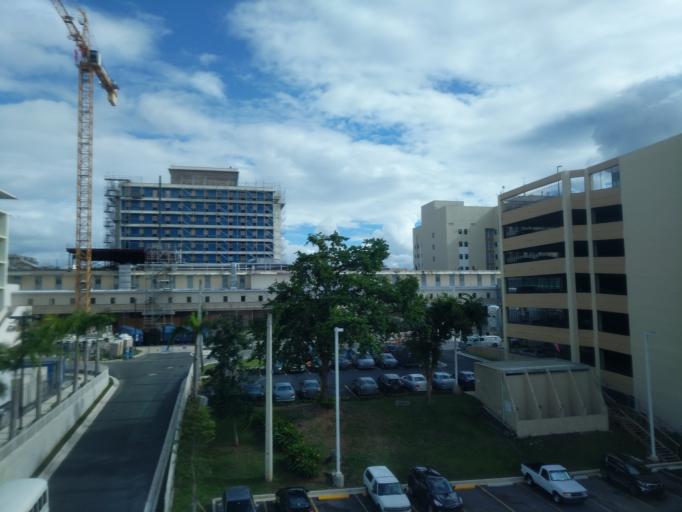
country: PR
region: Guaynabo
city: Guaynabo
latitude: 18.3911
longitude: -66.0807
